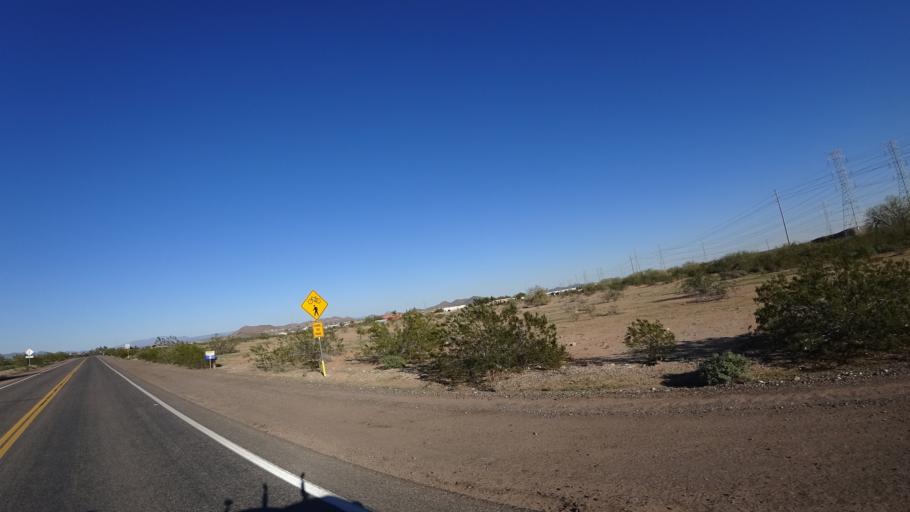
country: US
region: Arizona
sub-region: Maricopa County
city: Sun City West
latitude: 33.7074
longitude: -112.3108
